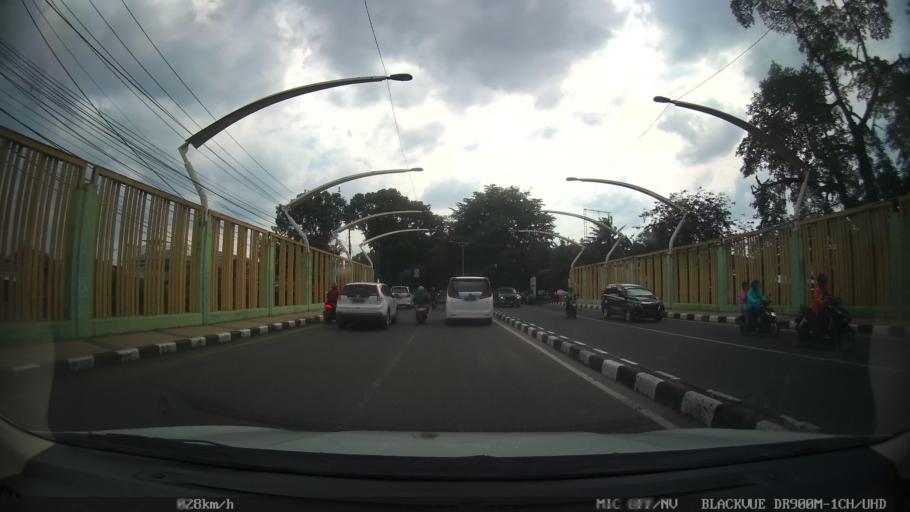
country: ID
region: North Sumatra
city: Medan
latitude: 3.5807
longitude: 98.6814
